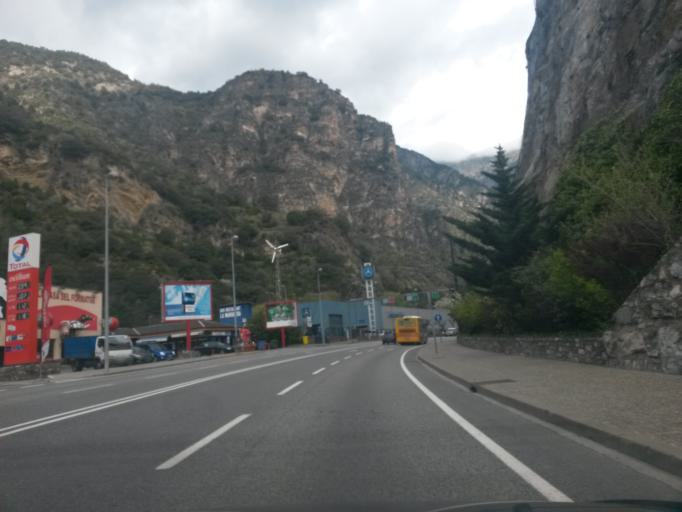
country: AD
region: Sant Julia de Loria
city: Sant Julia de Loria
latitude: 42.4790
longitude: 1.4897
